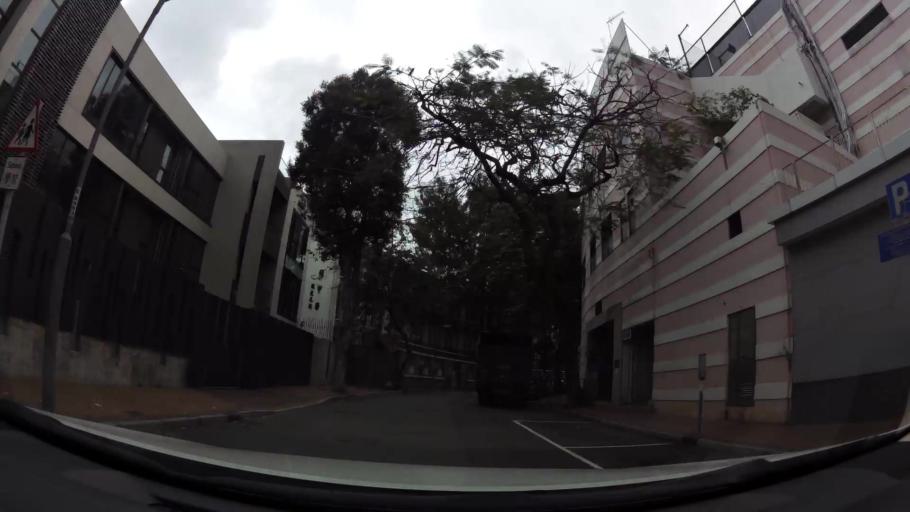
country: HK
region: Sham Shui Po
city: Sham Shui Po
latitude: 22.3309
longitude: 114.1730
